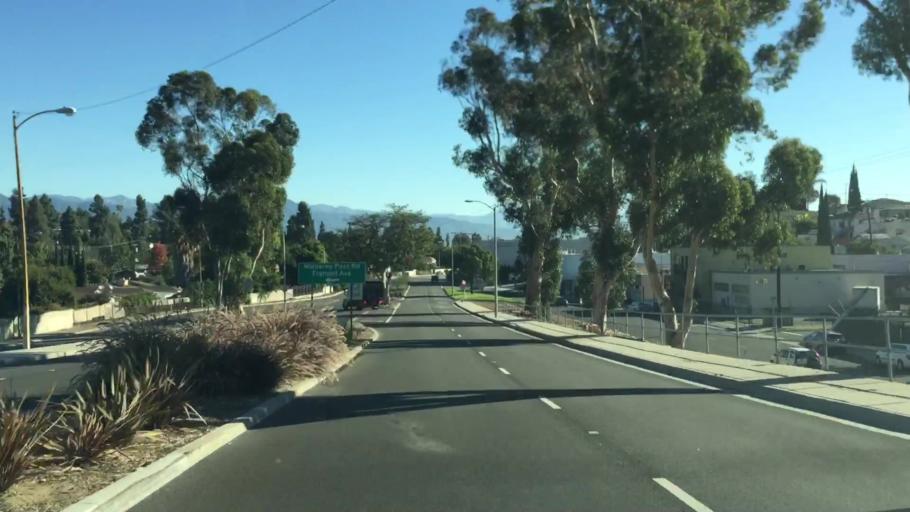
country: US
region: California
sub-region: Los Angeles County
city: Monterey Park
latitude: 34.0605
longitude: -118.1431
